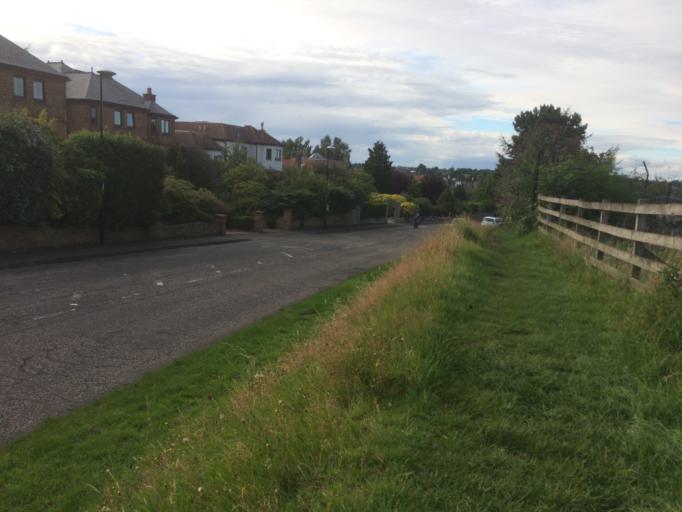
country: GB
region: Scotland
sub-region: Edinburgh
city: Edinburgh
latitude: 55.9221
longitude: -3.1998
